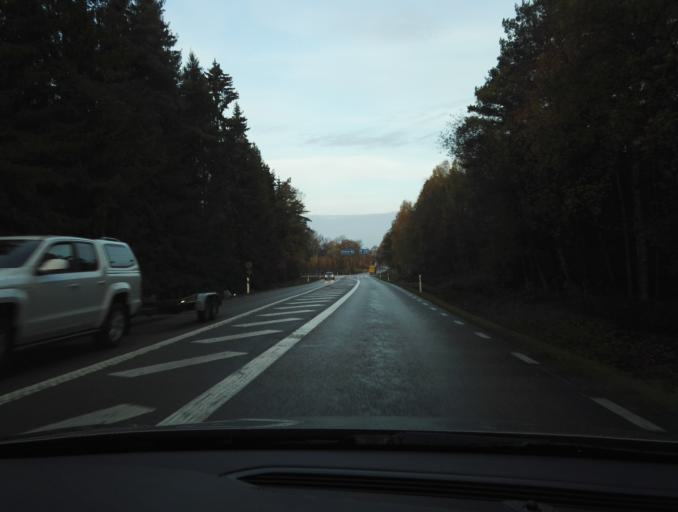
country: SE
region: Kronoberg
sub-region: Alvesta Kommun
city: Moheda
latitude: 56.9927
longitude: 14.6802
